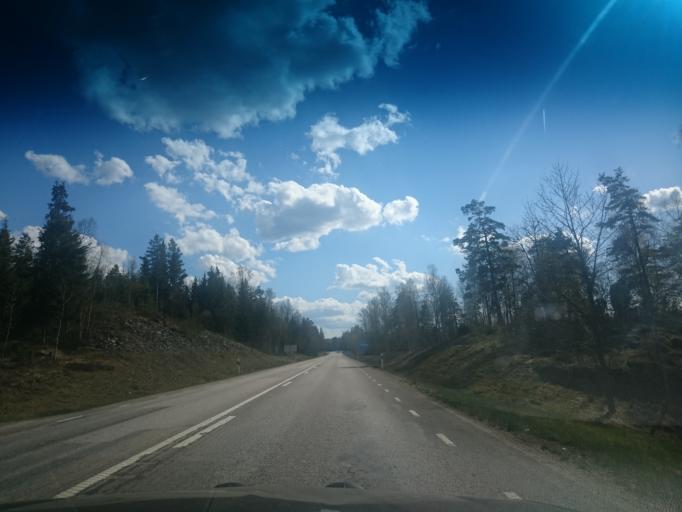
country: SE
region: Kronoberg
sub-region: Vaxjo Kommun
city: Braas
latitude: 57.2320
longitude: 15.1471
